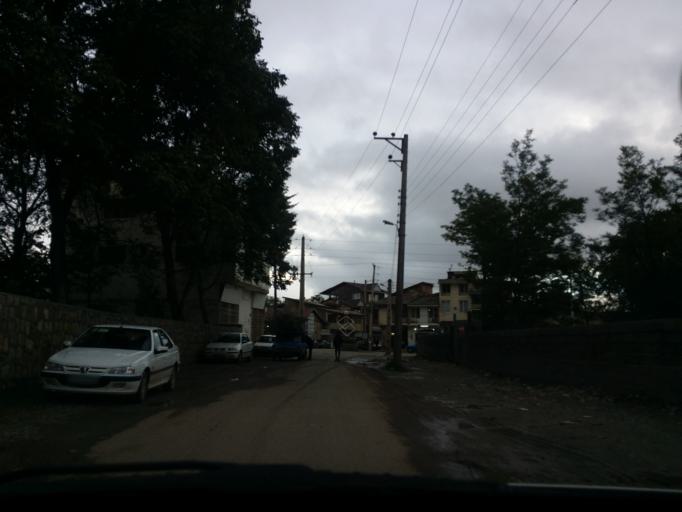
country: IR
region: Mazandaran
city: `Abbasabad
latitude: 36.5074
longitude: 51.1854
